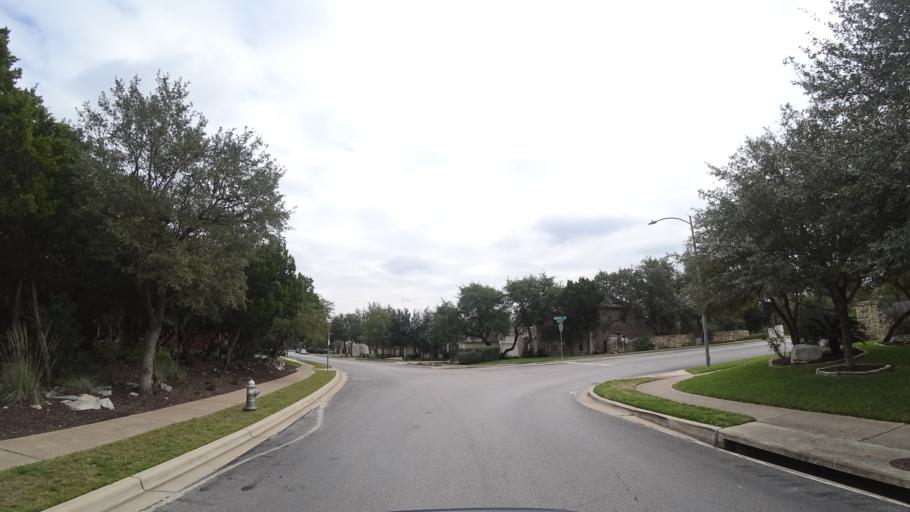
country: US
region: Texas
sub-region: Travis County
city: Shady Hollow
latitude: 30.2156
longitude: -97.8841
